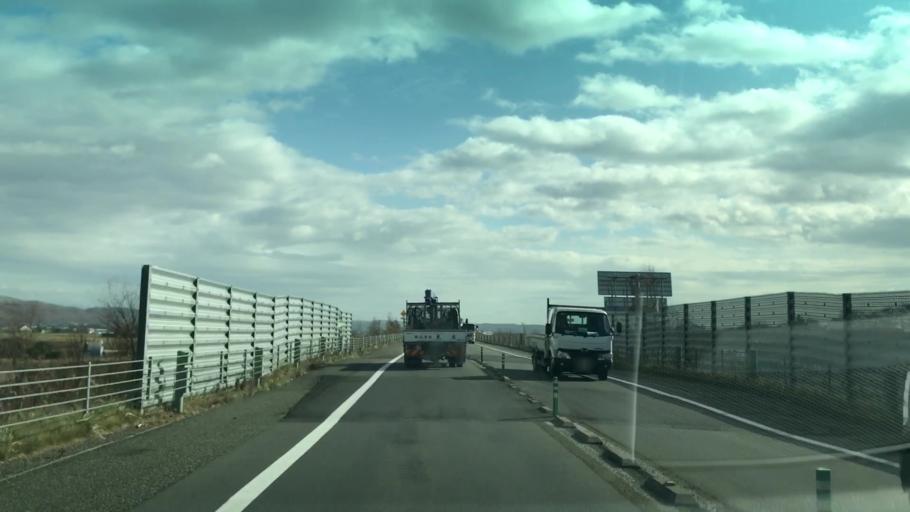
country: JP
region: Hokkaido
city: Tomakomai
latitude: 42.5798
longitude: 141.9525
